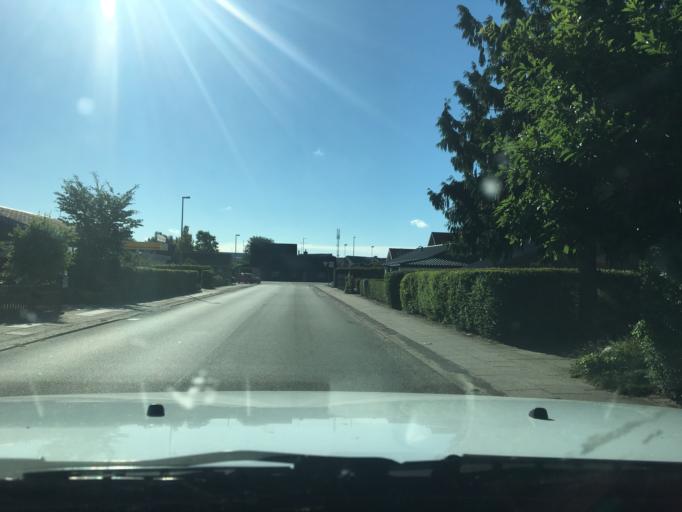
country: DK
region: Central Jutland
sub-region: Syddjurs Kommune
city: Hornslet
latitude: 56.3193
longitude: 10.3211
